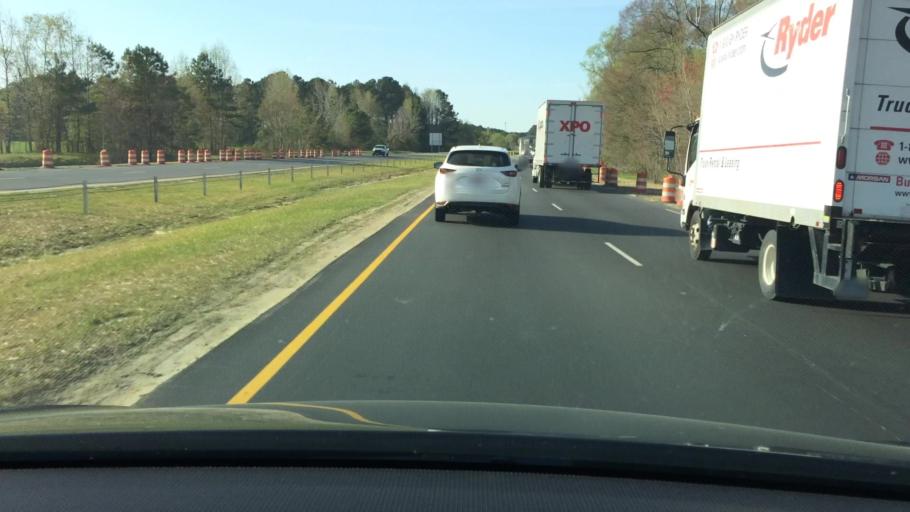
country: US
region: North Carolina
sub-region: Johnston County
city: Selma
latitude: 35.5003
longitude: -78.2799
